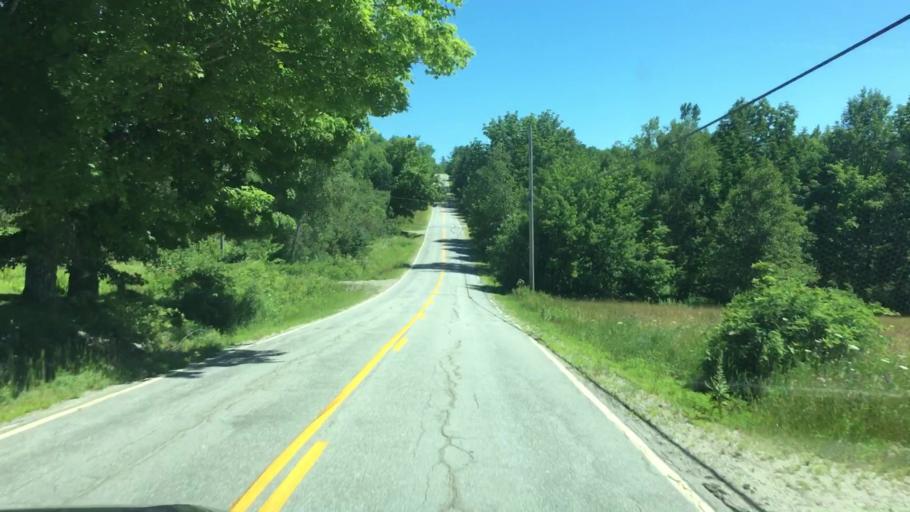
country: US
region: Maine
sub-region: Hancock County
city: Penobscot
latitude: 44.5195
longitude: -68.6654
